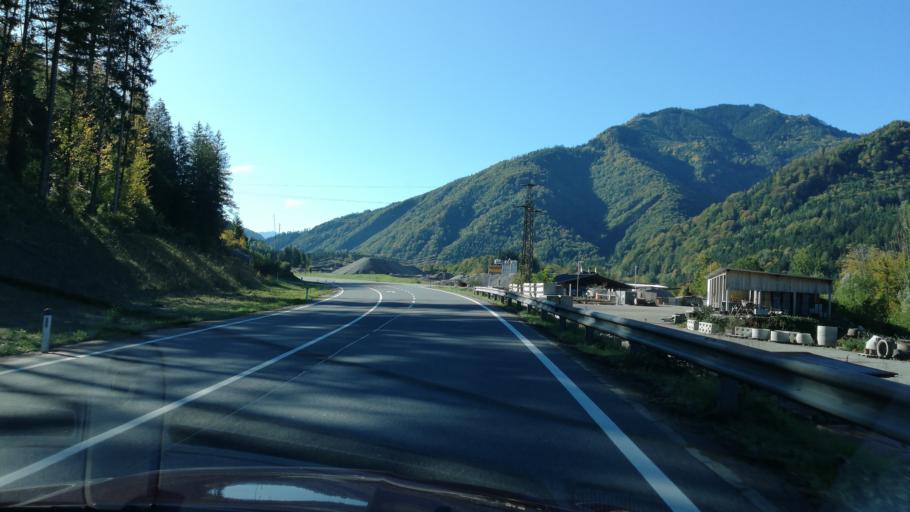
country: AT
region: Upper Austria
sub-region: Politischer Bezirk Steyr-Land
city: Weyer
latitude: 47.8034
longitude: 14.6460
